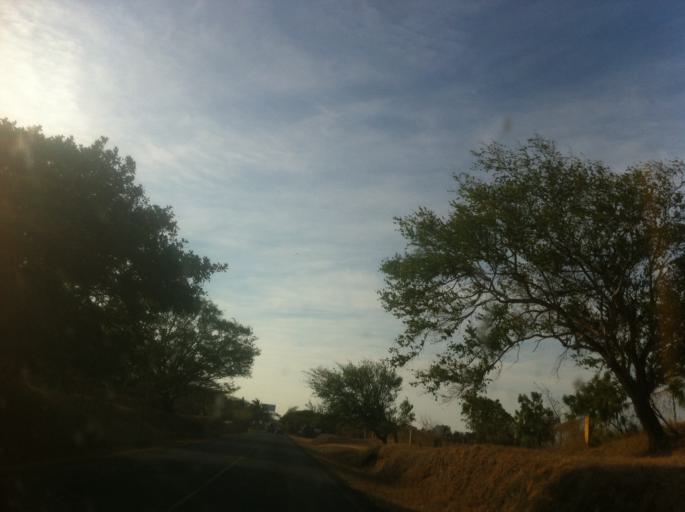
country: NI
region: Rivas
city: Rivas
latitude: 11.3510
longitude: -85.7387
